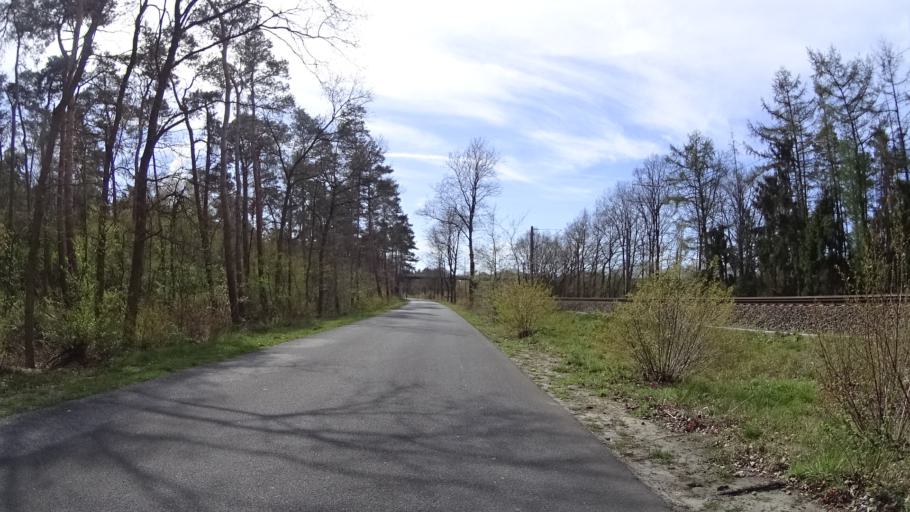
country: DE
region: Lower Saxony
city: Lingen
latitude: 52.4945
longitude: 7.3037
